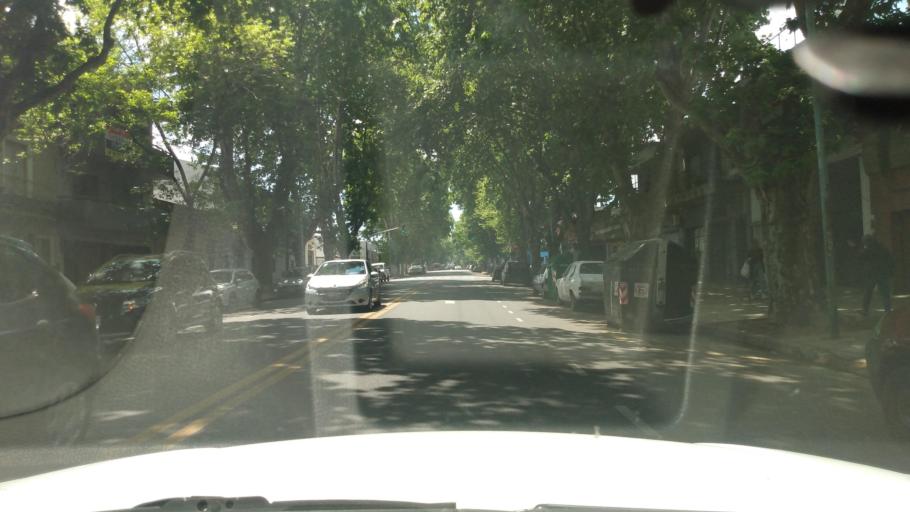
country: AR
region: Buenos Aires
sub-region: Partido de General San Martin
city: General San Martin
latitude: -34.5761
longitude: -58.5072
